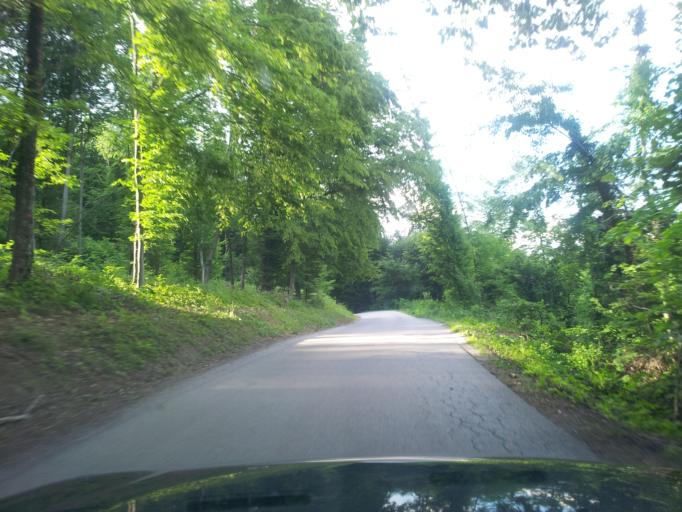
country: HR
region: Karlovacka
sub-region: Grad Karlovac
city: Karlovac
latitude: 45.4710
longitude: 15.4773
